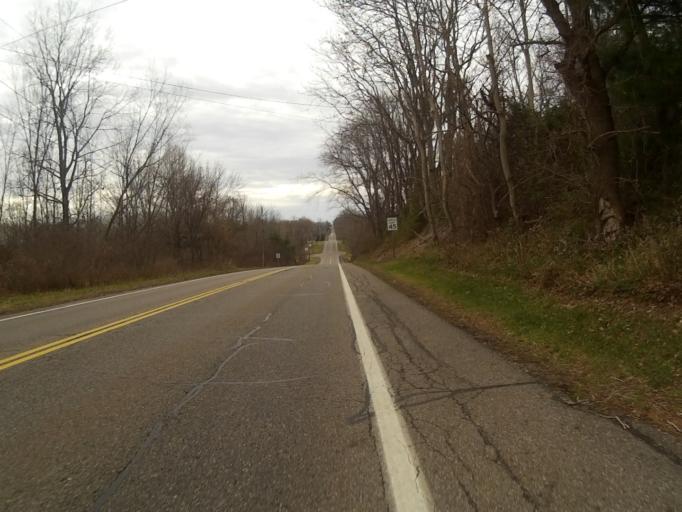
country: US
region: Ohio
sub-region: Summit County
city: Mogadore
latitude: 41.0470
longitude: -81.3473
